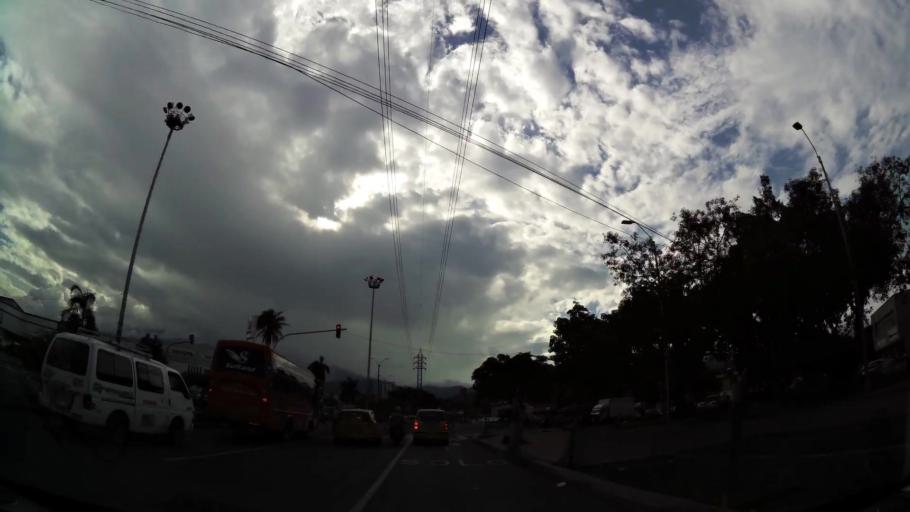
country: CO
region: Valle del Cauca
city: Cali
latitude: 3.4542
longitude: -76.5116
